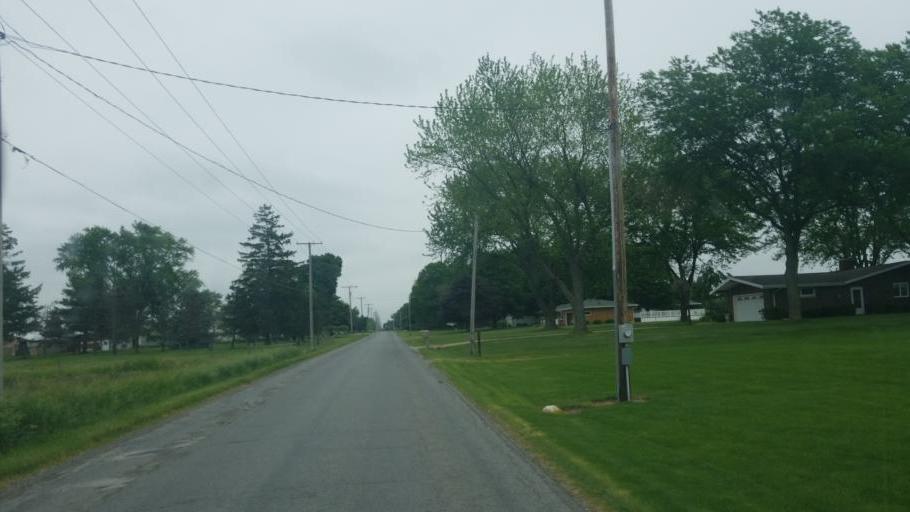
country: US
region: Indiana
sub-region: Elkhart County
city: Nappanee
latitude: 41.4572
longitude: -86.0116
